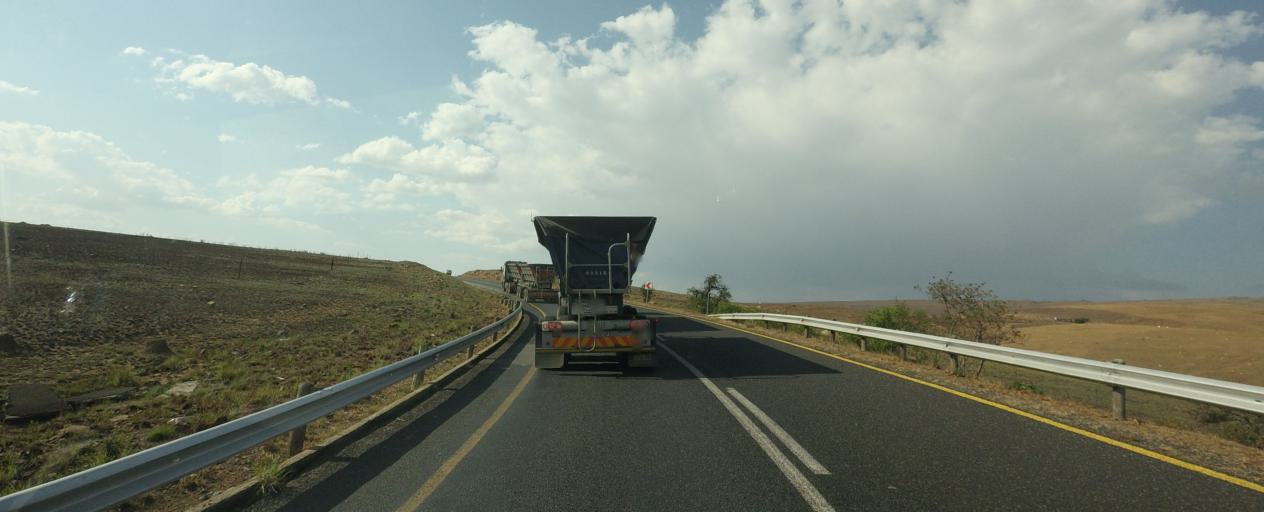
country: ZA
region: Mpumalanga
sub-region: Ehlanzeni District
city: Lydenburg
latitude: -25.1119
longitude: 30.5080
